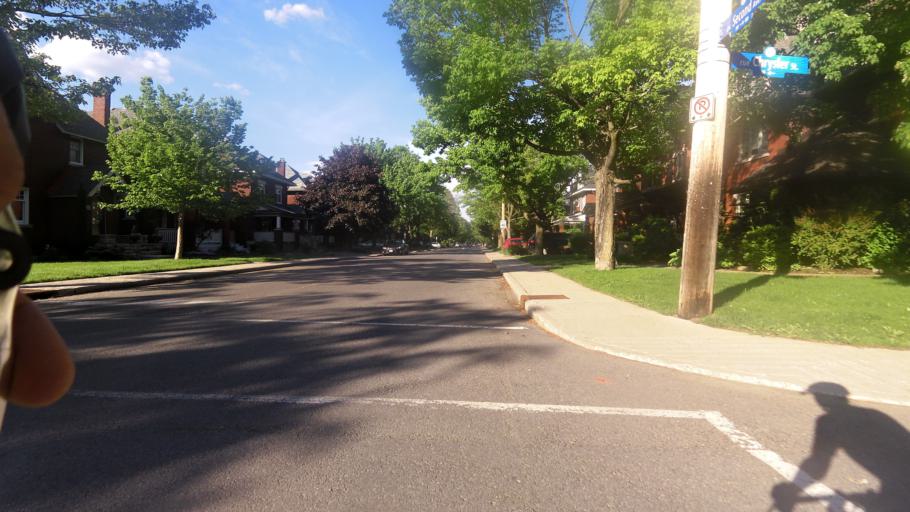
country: CA
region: Ontario
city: Ottawa
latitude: 45.4004
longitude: -75.6968
